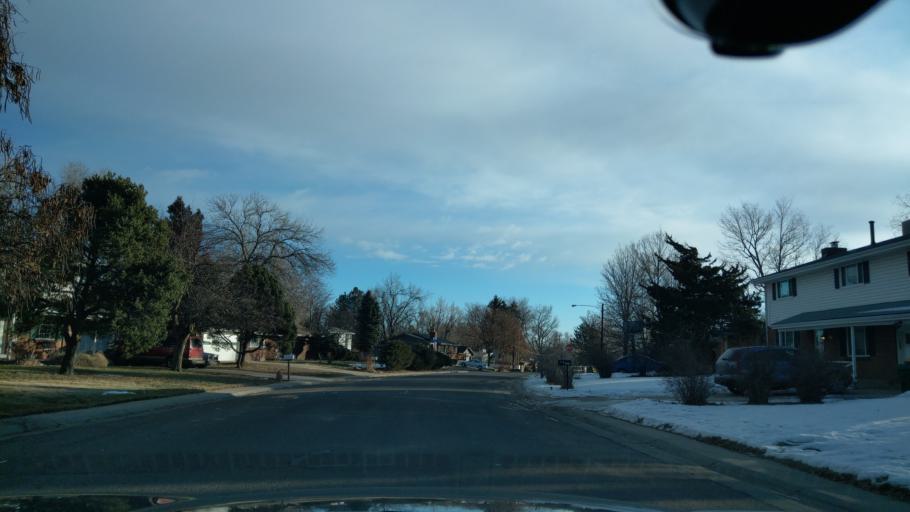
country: US
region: Colorado
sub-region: Jefferson County
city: Lakewood
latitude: 39.7306
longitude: -105.1159
